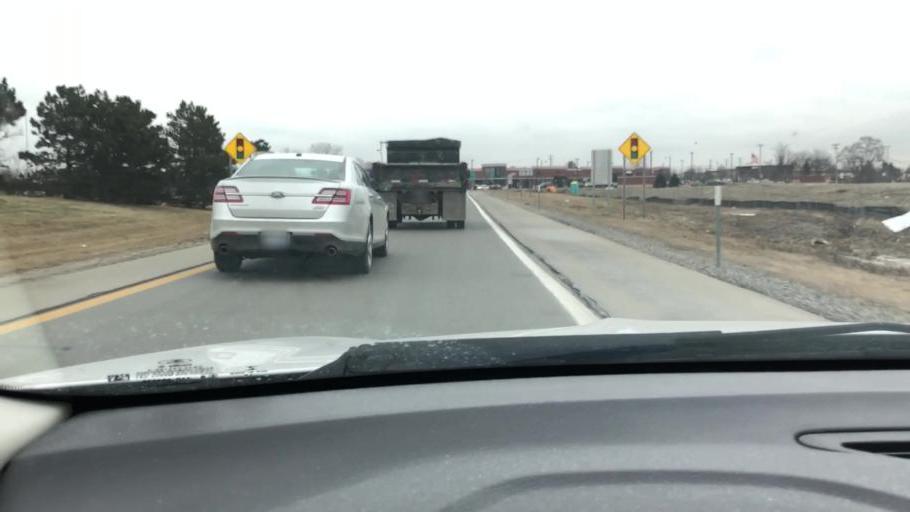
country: US
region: Michigan
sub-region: Oakland County
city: Novi
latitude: 42.4862
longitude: -83.4786
